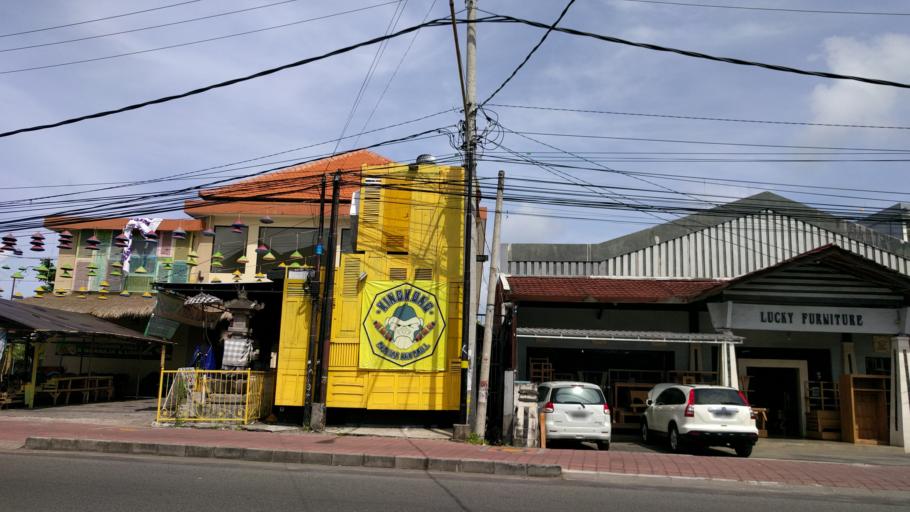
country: ID
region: Bali
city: Kuta
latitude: -8.7022
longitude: 115.1762
